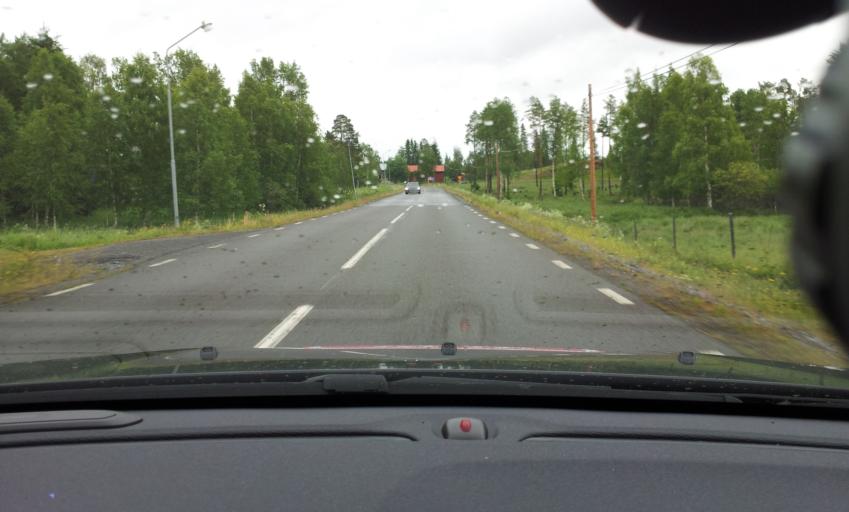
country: SE
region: Jaemtland
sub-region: OEstersunds Kommun
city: Lit
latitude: 63.6701
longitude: 15.0929
